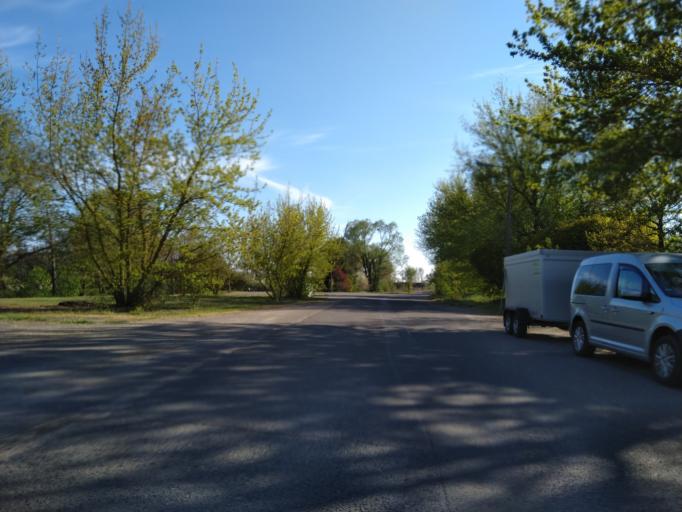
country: DE
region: Brandenburg
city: Neutrebbin
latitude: 52.7158
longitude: 14.2104
